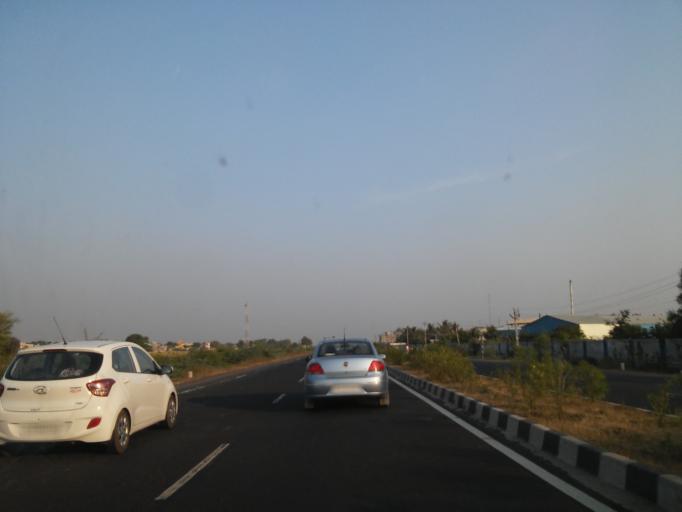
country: IN
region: Gujarat
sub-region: Ahmadabad
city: Sanand
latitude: 23.0456
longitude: 72.2572
